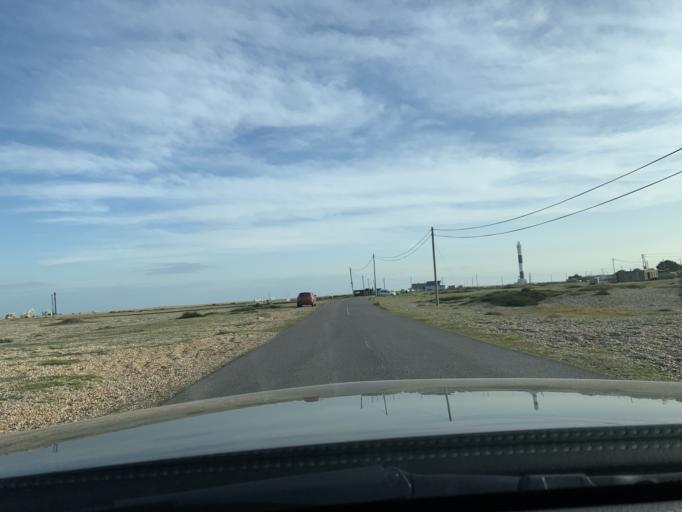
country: GB
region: England
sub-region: Kent
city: New Romney
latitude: 50.9181
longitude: 0.9768
